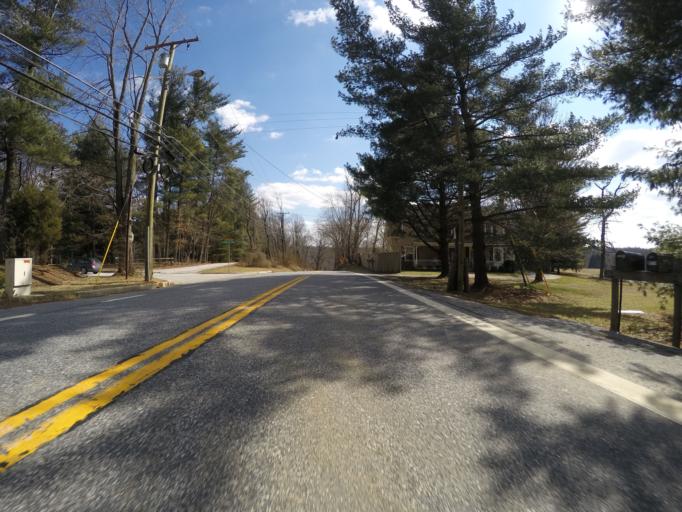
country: US
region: Maryland
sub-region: Baltimore County
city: Mays Chapel
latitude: 39.4496
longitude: -76.6861
